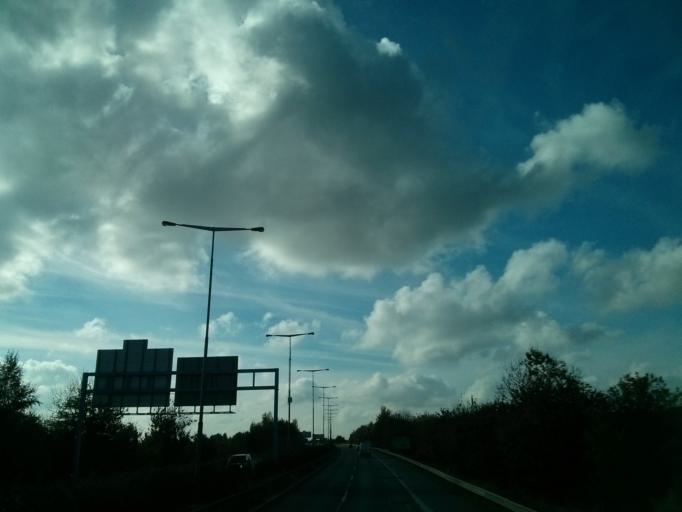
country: CZ
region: Central Bohemia
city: Hostivice
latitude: 50.0489
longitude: 14.2656
